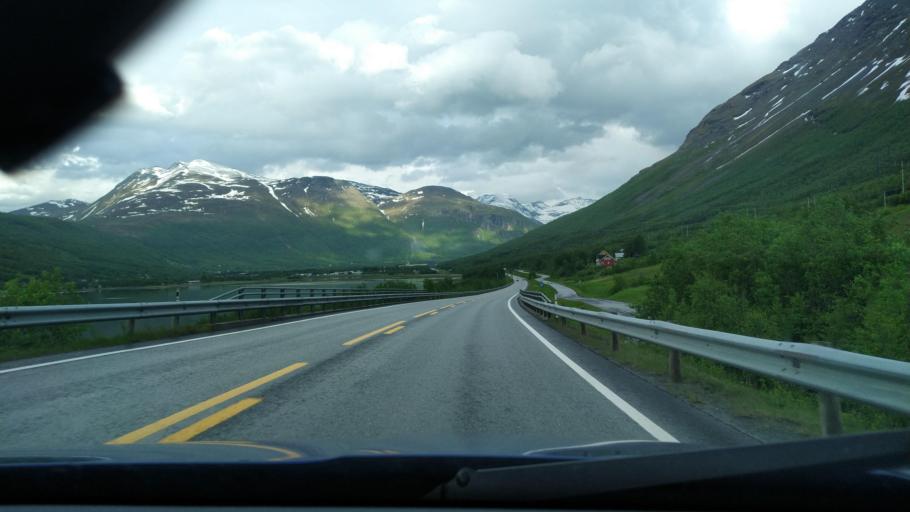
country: NO
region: Troms
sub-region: Balsfjord
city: Storsteinnes
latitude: 69.2152
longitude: 19.5034
